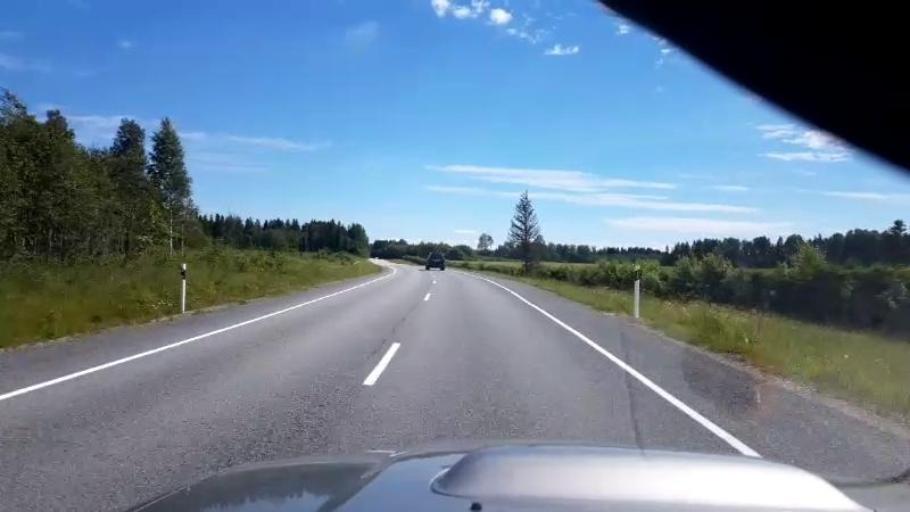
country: EE
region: Jaervamaa
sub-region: Jaerva-Jaani vald
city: Jarva-Jaani
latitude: 59.0204
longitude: 25.9031
